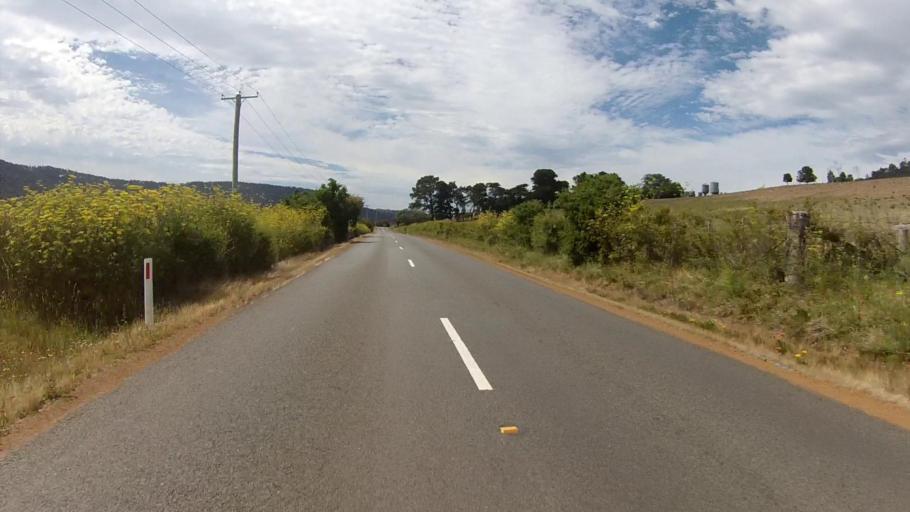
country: AU
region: Tasmania
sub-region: Brighton
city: Old Beach
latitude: -42.7011
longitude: 147.3603
